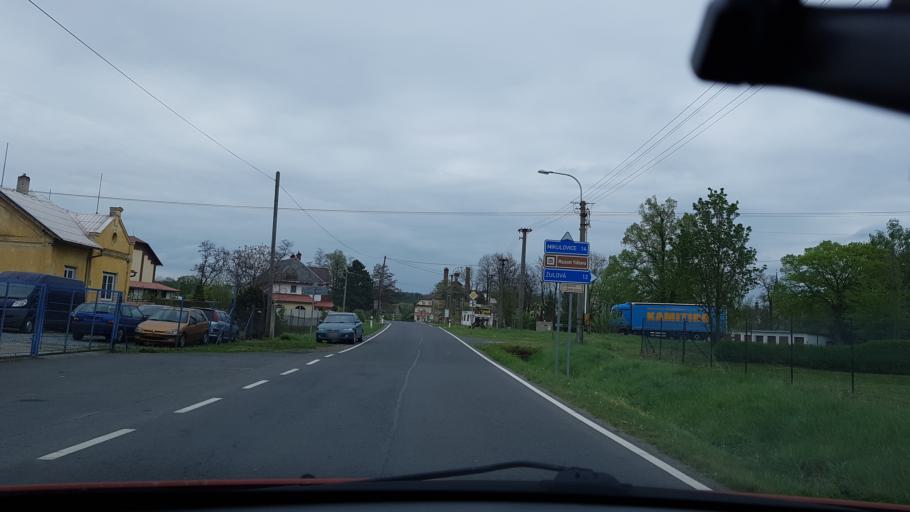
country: CZ
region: Olomoucky
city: Vidnava
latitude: 50.3740
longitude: 17.1802
